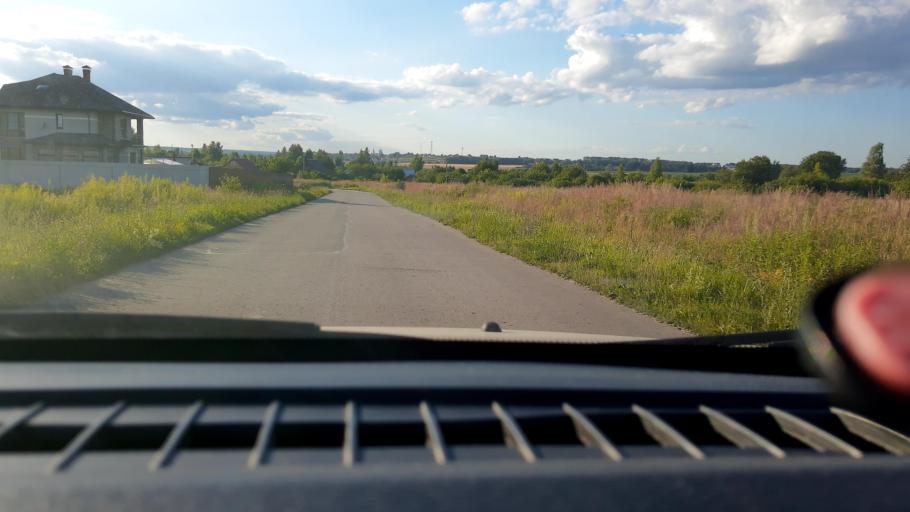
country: RU
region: Nizjnij Novgorod
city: Burevestnik
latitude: 56.0421
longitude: 43.8830
